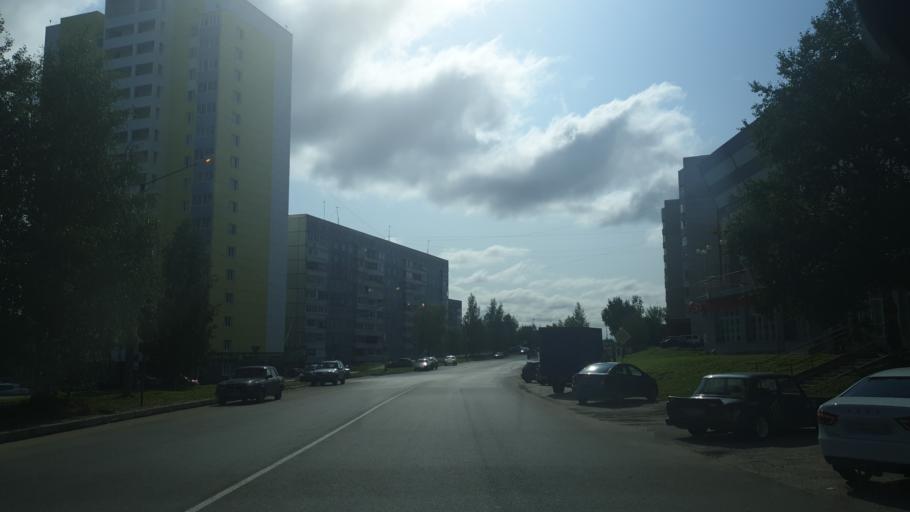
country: RU
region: Komi Republic
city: Ezhva
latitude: 61.7856
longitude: 50.7569
